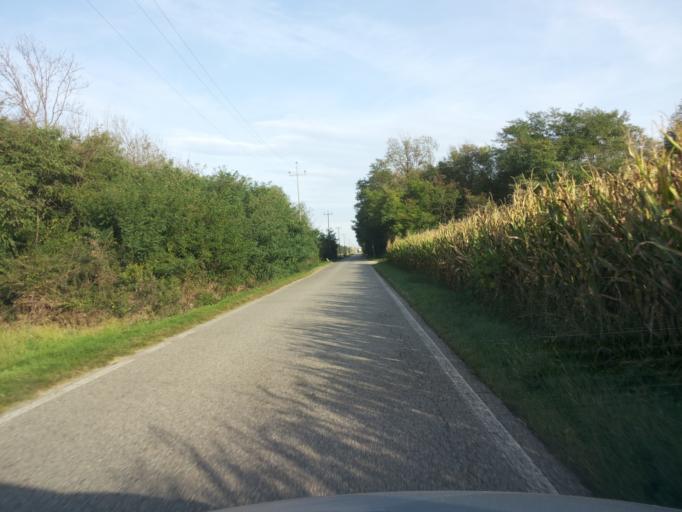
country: IT
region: Piedmont
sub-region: Provincia di Biella
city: Salussola
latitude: 45.4483
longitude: 8.1270
